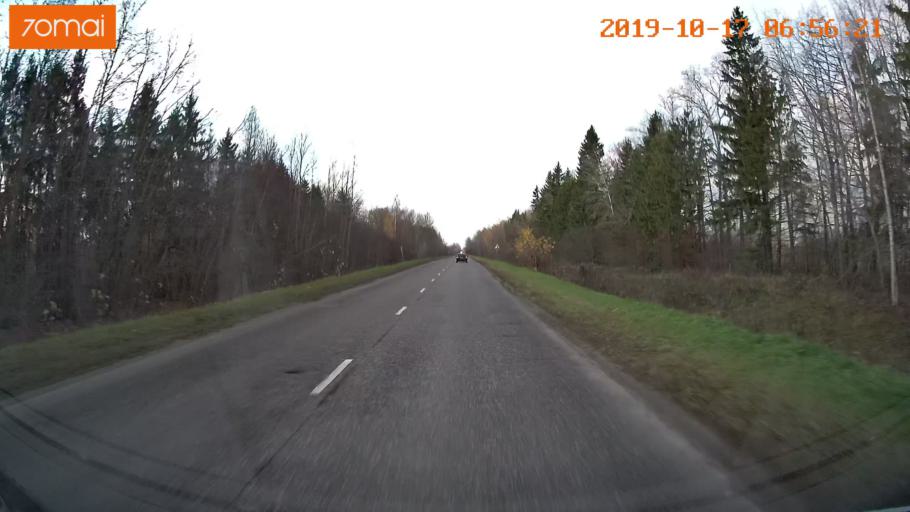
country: RU
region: Vladimir
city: Suzdal'
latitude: 56.4476
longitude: 40.4485
